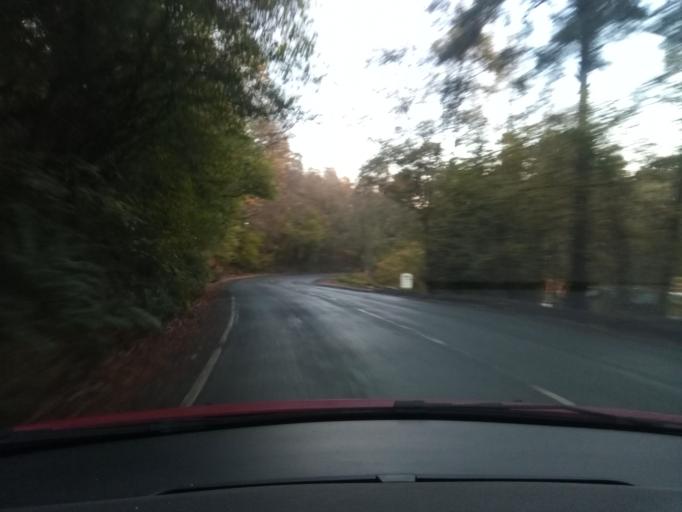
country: GB
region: England
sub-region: Northumberland
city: Bardon Mill
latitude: 54.9484
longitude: -2.2684
